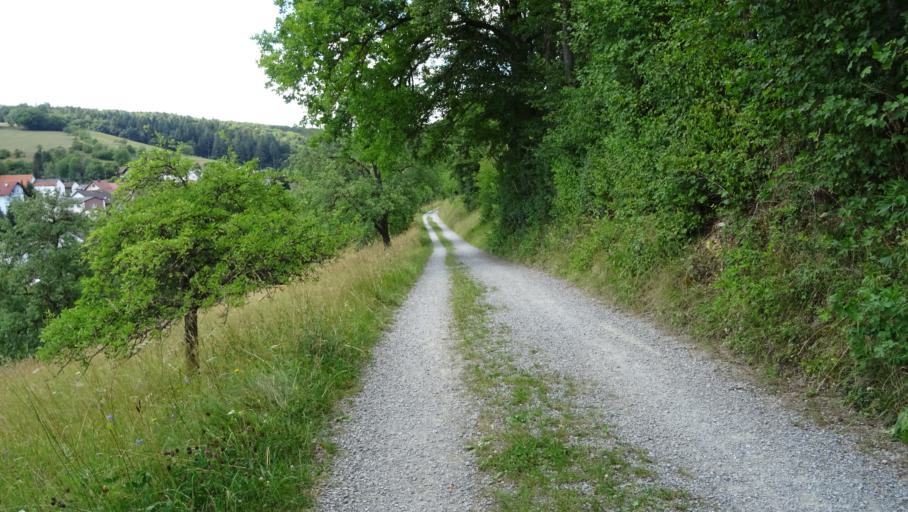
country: DE
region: Baden-Wuerttemberg
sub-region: Karlsruhe Region
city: Mosbach
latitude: 49.3707
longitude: 9.1279
